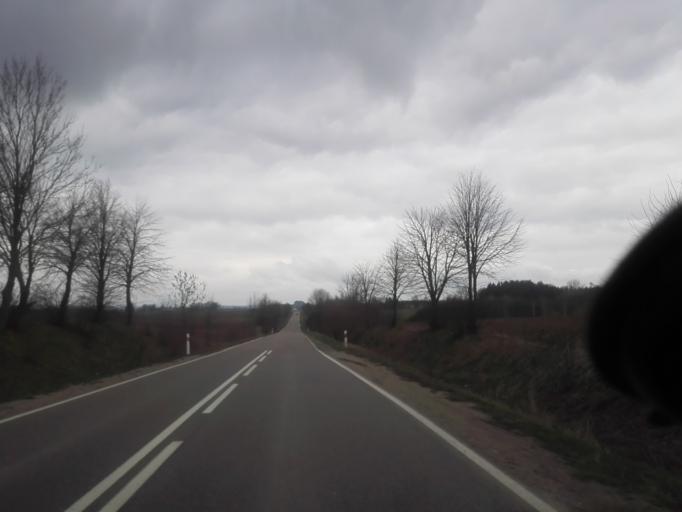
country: PL
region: Podlasie
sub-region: Suwalki
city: Suwalki
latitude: 54.2168
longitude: 22.9121
